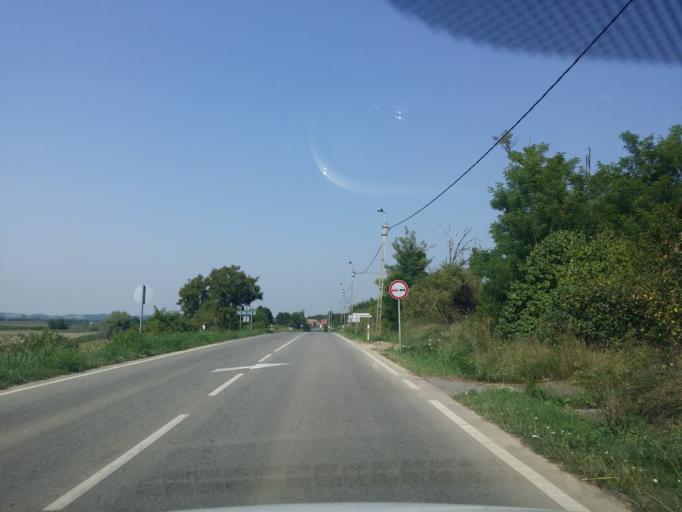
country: HU
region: Tolna
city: Pincehely
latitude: 46.7061
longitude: 18.4705
